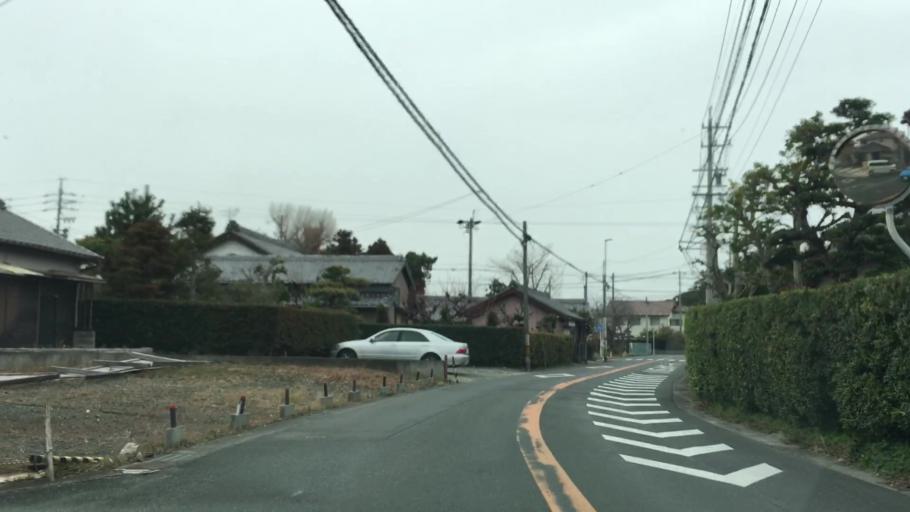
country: JP
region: Aichi
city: Toyohashi
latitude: 34.7397
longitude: 137.3676
